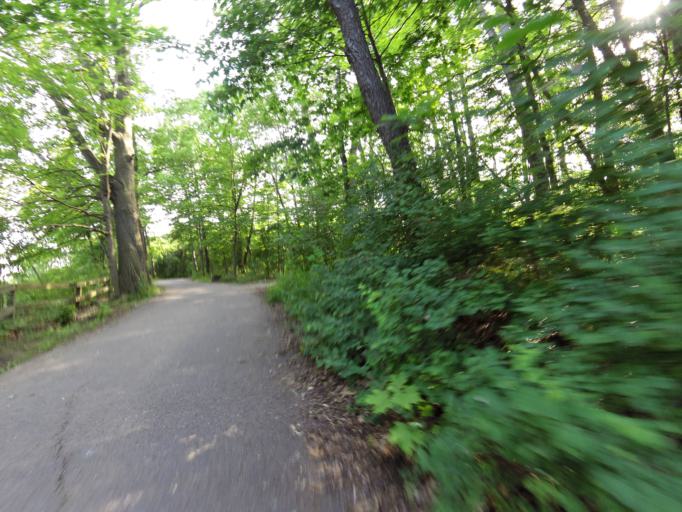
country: CA
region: Ontario
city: Etobicoke
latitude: 43.6670
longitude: -79.5133
